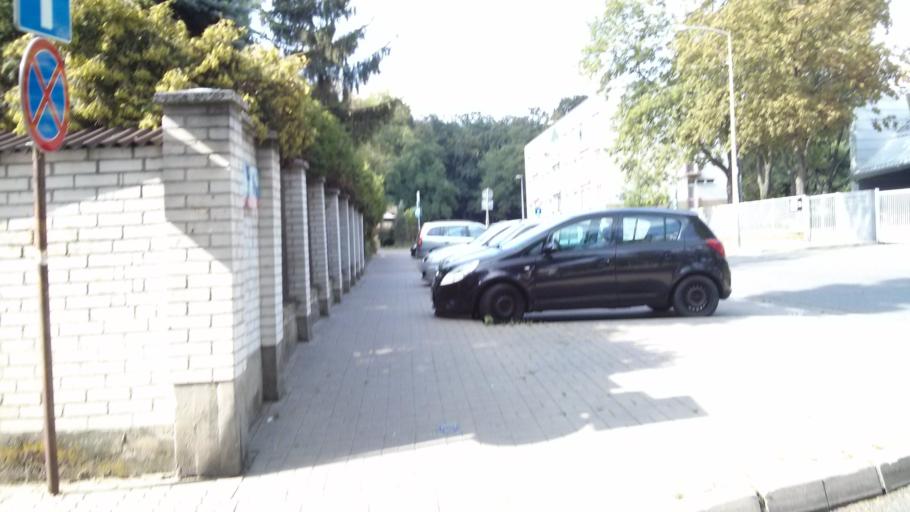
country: PL
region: Masovian Voivodeship
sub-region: Warszawa
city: Wola
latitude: 52.2481
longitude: 20.9531
